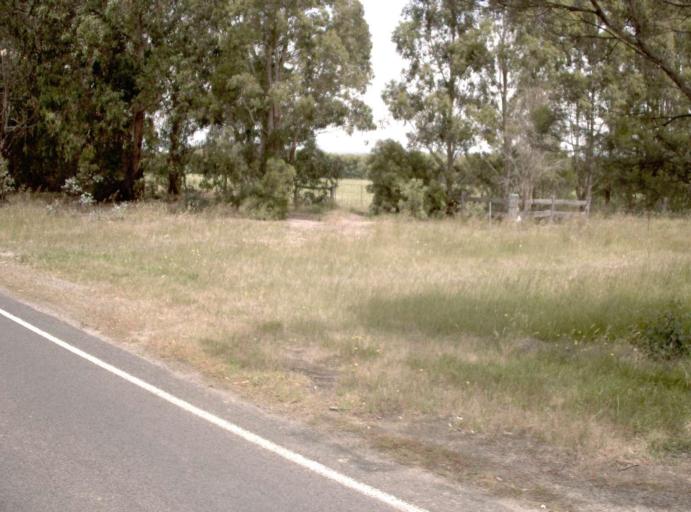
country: AU
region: Victoria
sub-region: Latrobe
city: Traralgon
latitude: -38.4911
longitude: 146.7132
